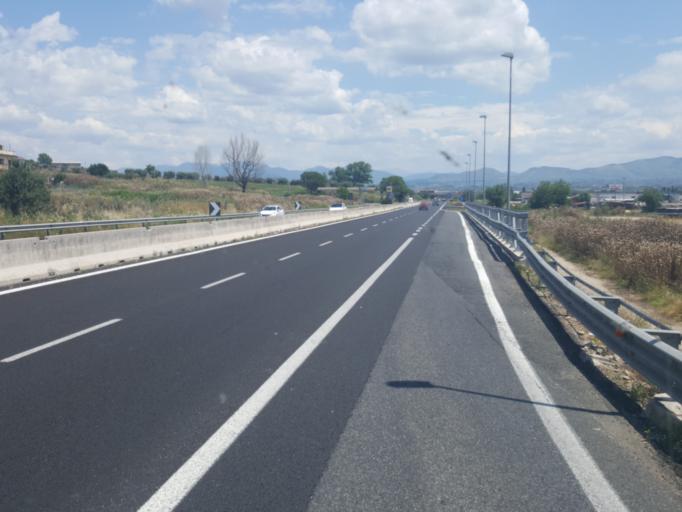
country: IT
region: Latium
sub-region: Citta metropolitana di Roma Capitale
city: Fiano Romano
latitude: 42.1421
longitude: 12.6126
